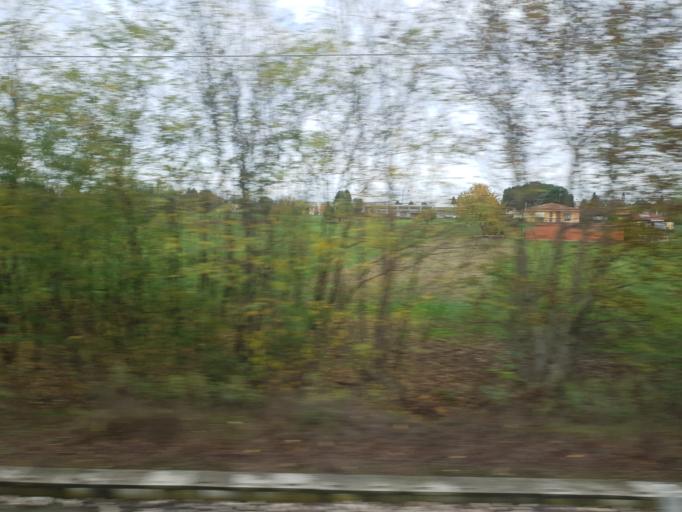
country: IT
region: Lombardy
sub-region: Provincia di Varese
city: Ferno
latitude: 45.6024
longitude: 8.7750
